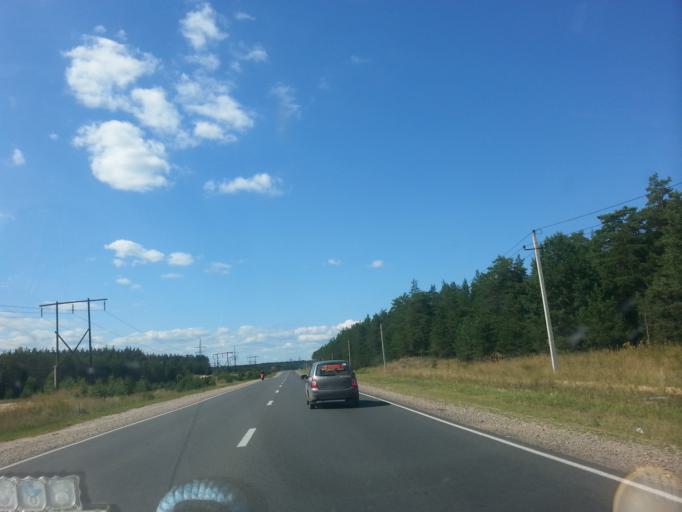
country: RU
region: Nizjnij Novgorod
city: Lukino
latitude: 56.3989
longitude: 43.6670
